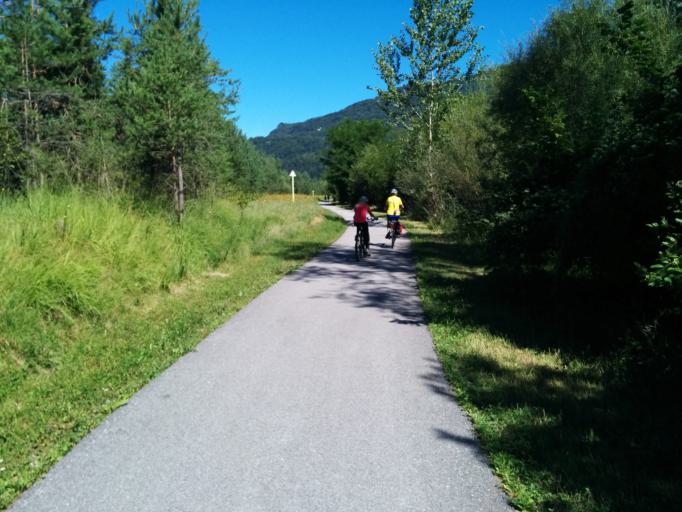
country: IT
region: Friuli Venezia Giulia
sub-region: Provincia di Udine
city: Villa Santina
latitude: 46.4137
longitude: 12.9085
